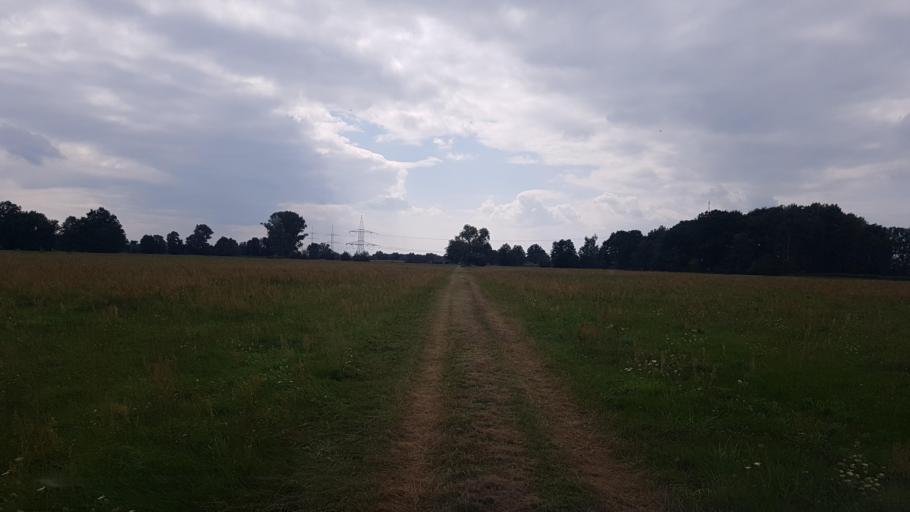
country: DE
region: Brandenburg
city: Ruckersdorf
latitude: 51.5964
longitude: 13.5388
